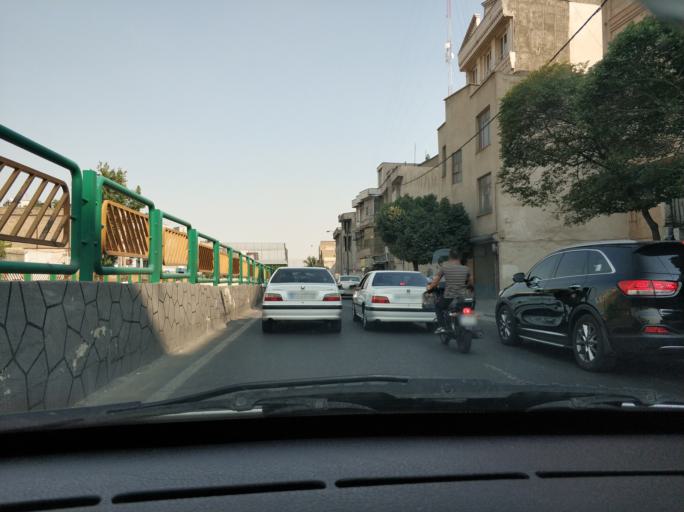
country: IR
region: Tehran
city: Tehran
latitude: 35.7338
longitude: 51.4607
